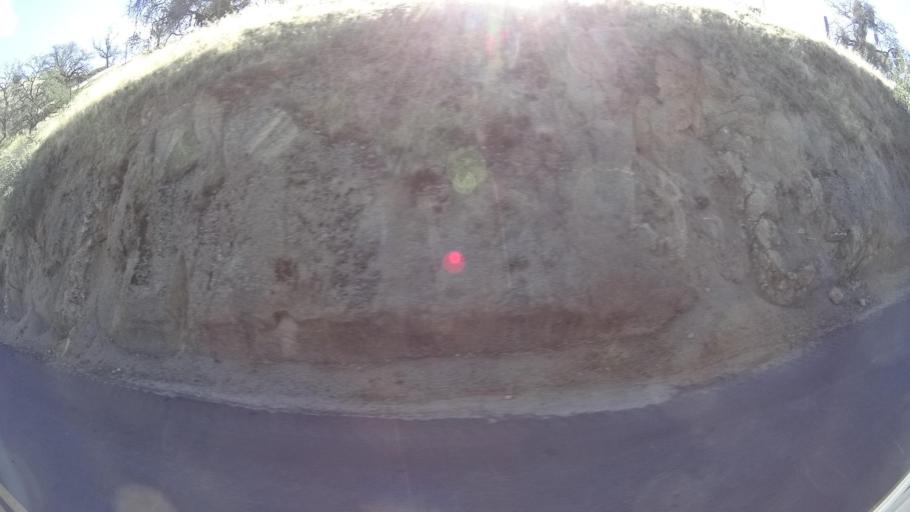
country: US
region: California
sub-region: Tulare County
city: Richgrove
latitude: 35.6933
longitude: -118.8673
